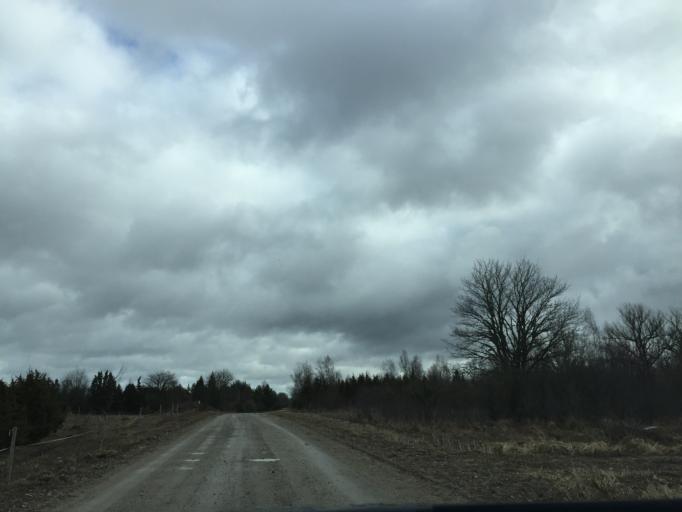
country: EE
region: Laeaene
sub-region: Haapsalu linn
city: Haapsalu
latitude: 58.6848
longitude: 23.5432
